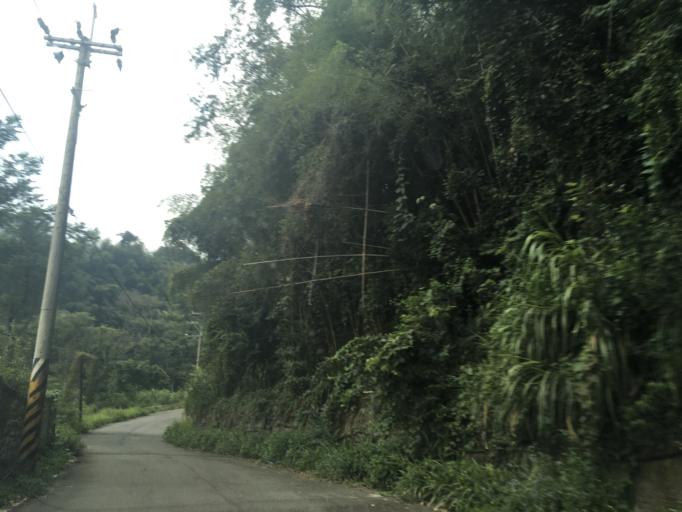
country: TW
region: Taiwan
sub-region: Miaoli
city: Miaoli
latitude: 24.3956
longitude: 120.9783
